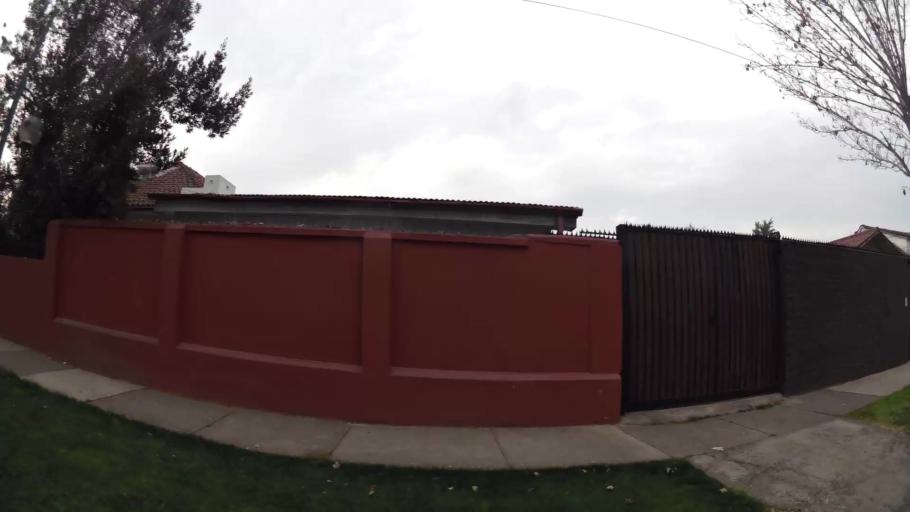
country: CL
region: Santiago Metropolitan
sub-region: Provincia de Santiago
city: Villa Presidente Frei, Nunoa, Santiago, Chile
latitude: -33.4725
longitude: -70.6022
